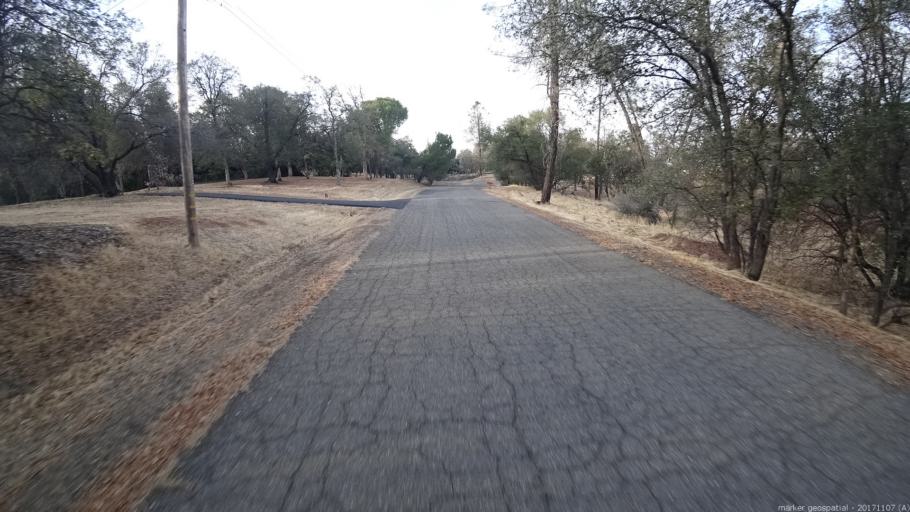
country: US
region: California
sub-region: Shasta County
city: Shasta
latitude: 40.5339
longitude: -122.4807
